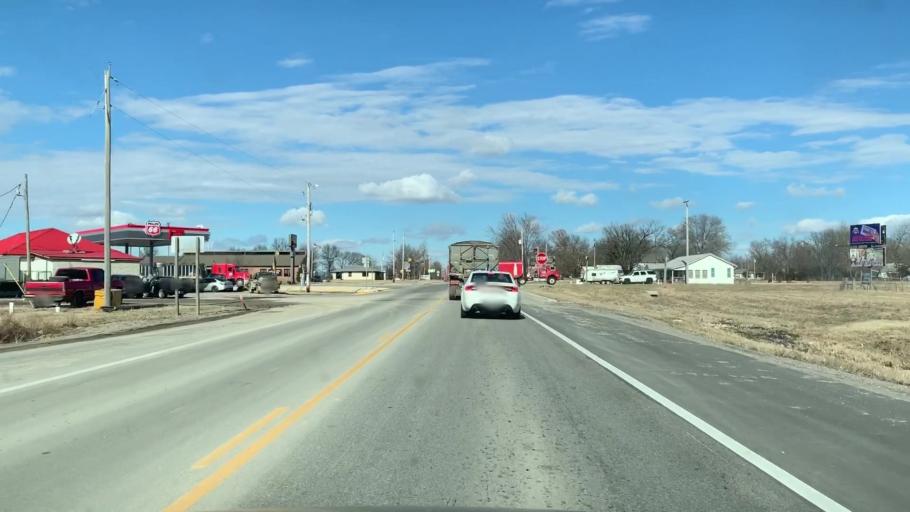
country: US
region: Kansas
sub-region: Crawford County
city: Pittsburg
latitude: 37.3386
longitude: -94.8322
